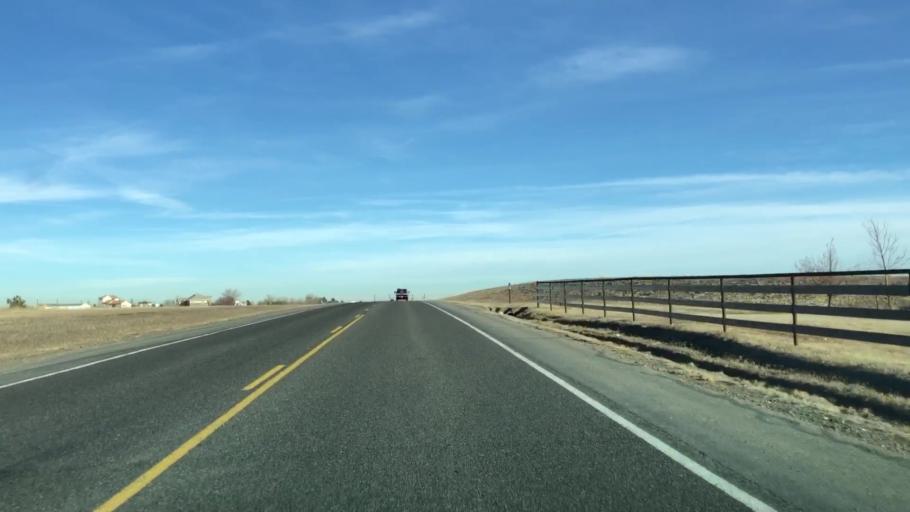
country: US
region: Colorado
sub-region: Weld County
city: Windsor
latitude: 40.4296
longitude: -104.9442
